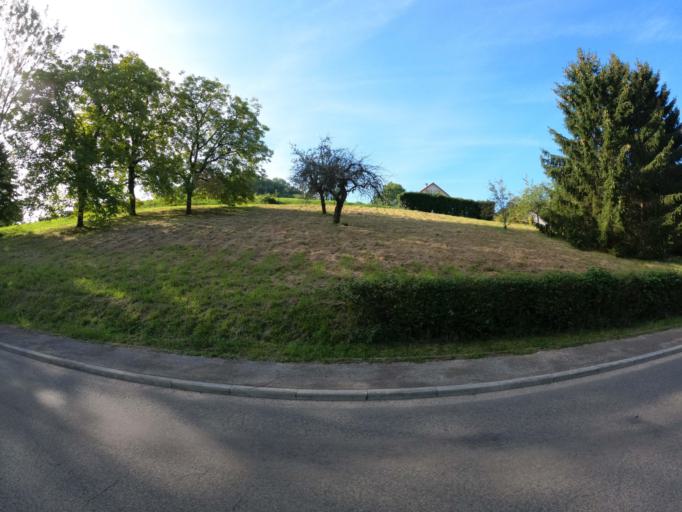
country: FR
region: Franche-Comte
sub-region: Departement du Jura
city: Montmorot
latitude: 46.7178
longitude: 5.5311
